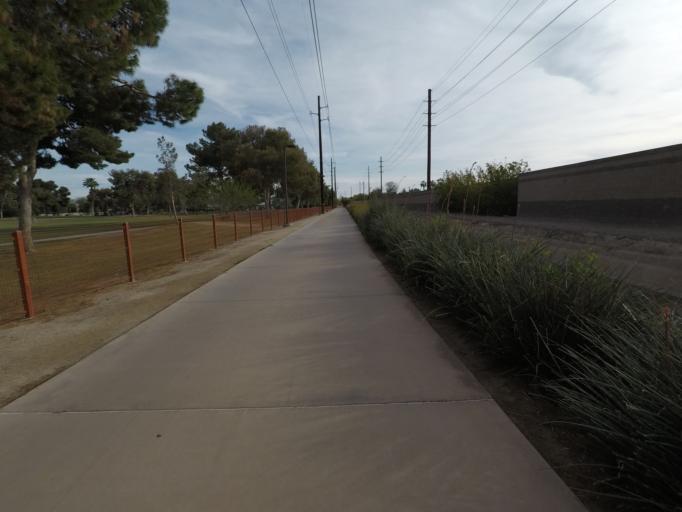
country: US
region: Arizona
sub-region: Maricopa County
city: Guadalupe
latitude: 33.3509
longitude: -111.9382
